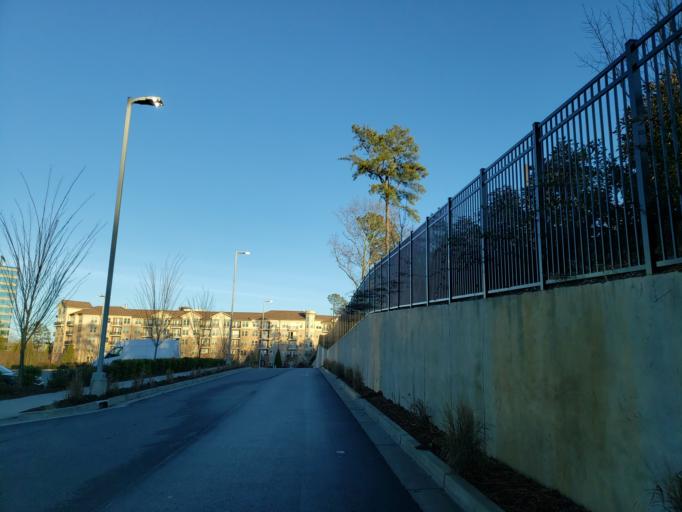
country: US
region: Georgia
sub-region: Fulton County
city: Sandy Springs
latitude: 33.9324
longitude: -84.3634
